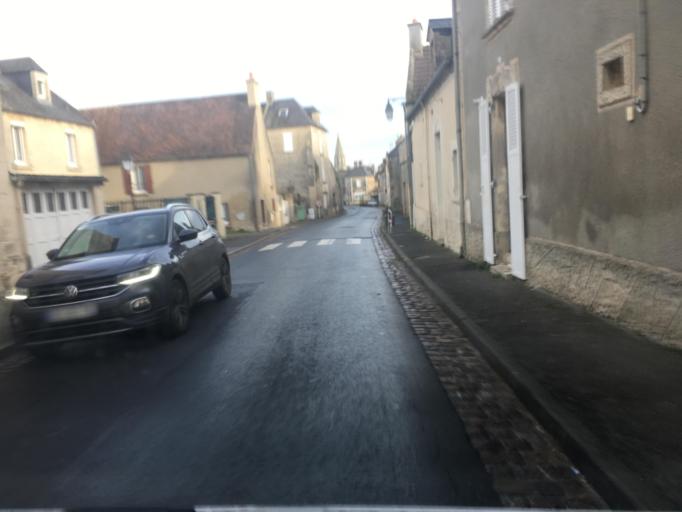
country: FR
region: Lower Normandy
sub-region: Departement du Calvados
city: Creully
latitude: 49.2828
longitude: -0.5424
